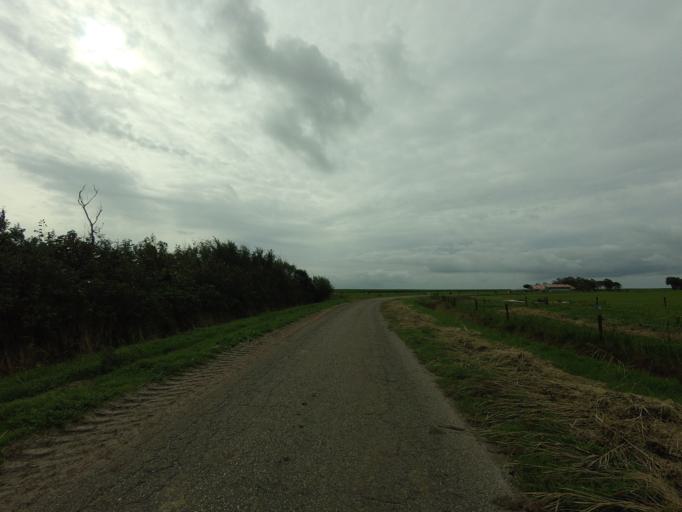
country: NL
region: Friesland
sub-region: Gemeente Ameland
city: Nes
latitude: 53.4358
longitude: 5.7064
